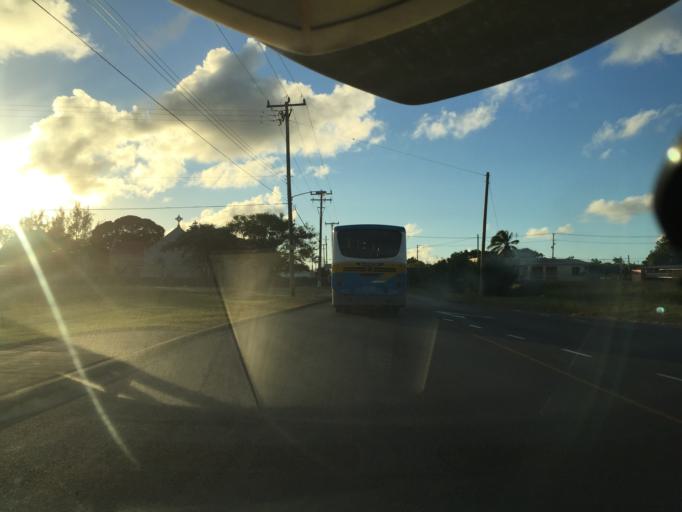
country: BB
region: Christ Church
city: Oistins
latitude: 13.0803
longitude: -59.4920
